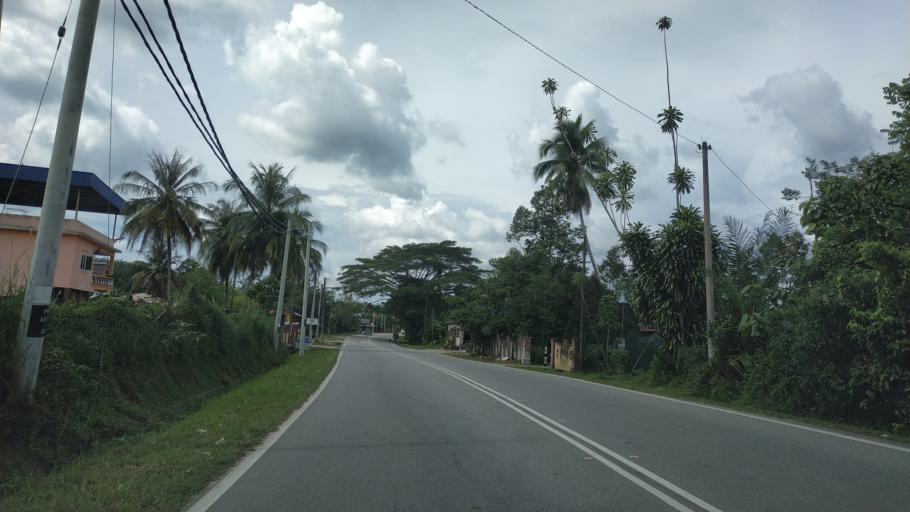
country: MY
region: Kedah
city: Kulim
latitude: 5.4250
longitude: 100.6636
